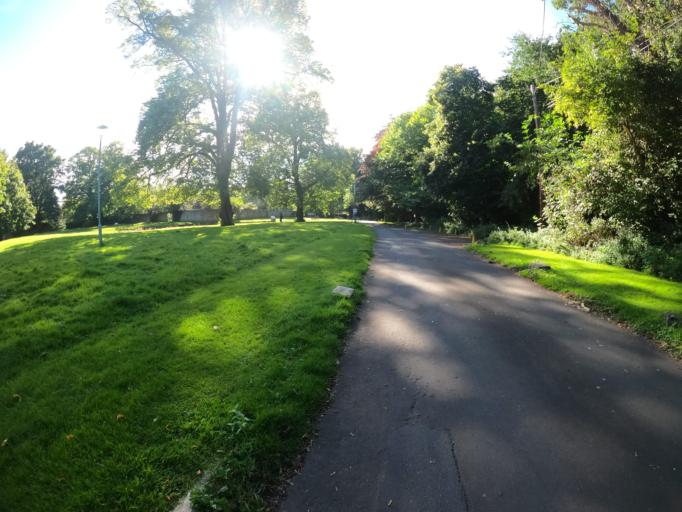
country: GB
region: Scotland
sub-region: Fife
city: Aberdour
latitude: 55.9784
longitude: -3.2987
